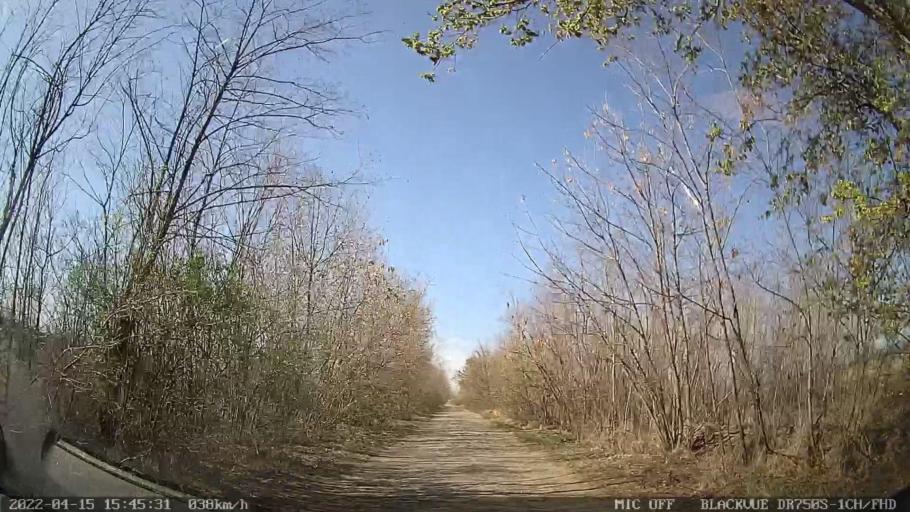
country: MD
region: Raionul Ocnita
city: Otaci
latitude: 48.3767
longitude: 27.9180
